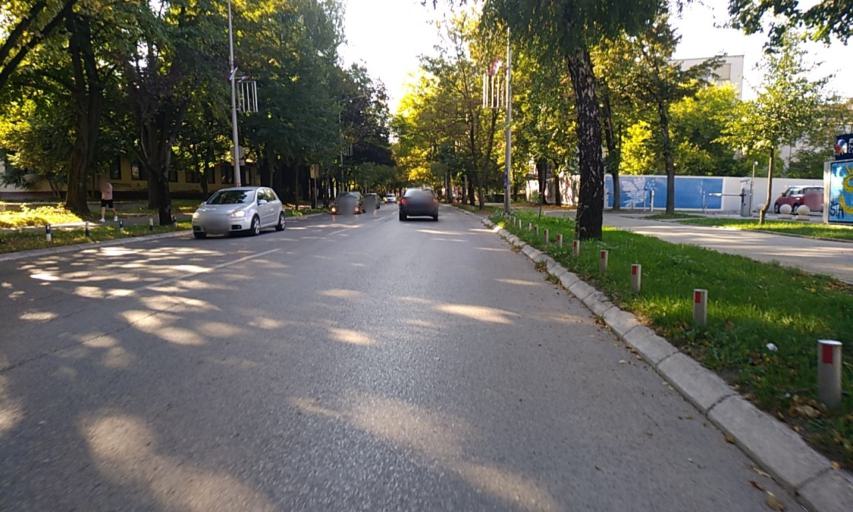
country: BA
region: Republika Srpska
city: Banja Luka
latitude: 44.7757
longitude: 17.1911
